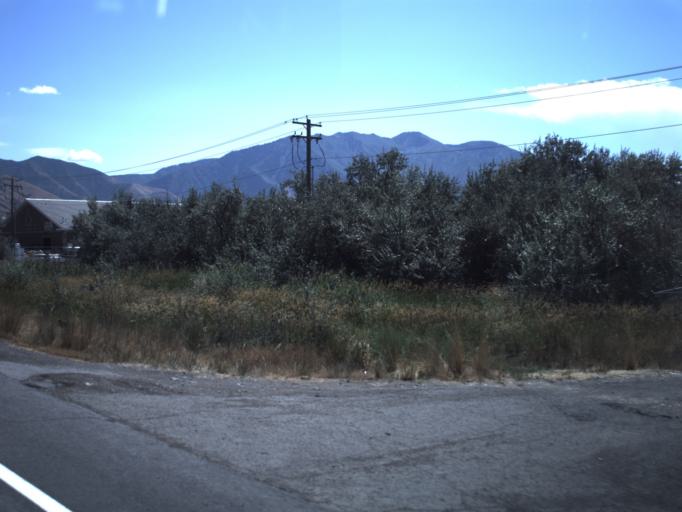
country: US
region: Utah
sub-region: Utah County
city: Springville
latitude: 40.1867
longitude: -111.6243
